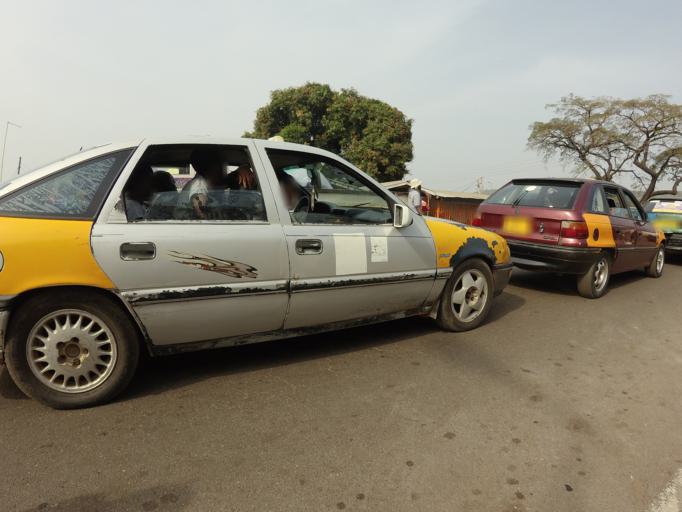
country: GH
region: Volta
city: Ho
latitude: 6.6166
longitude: 0.4731
